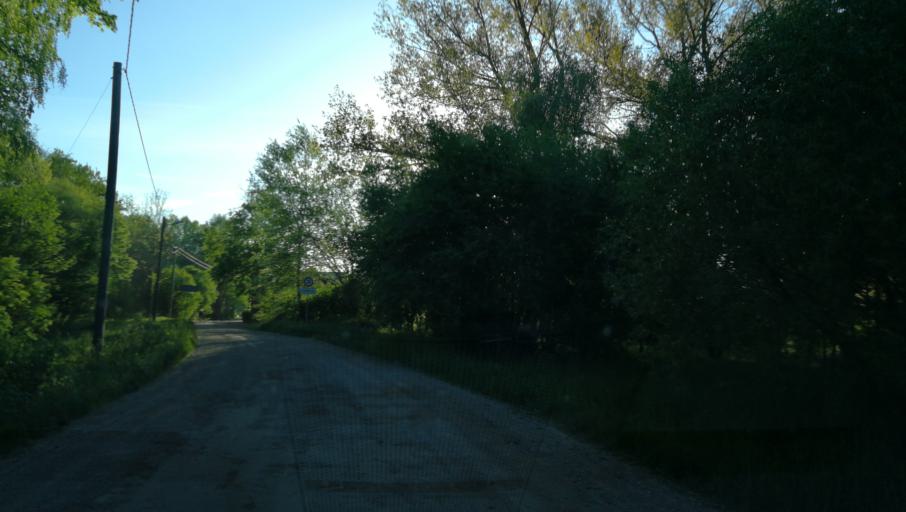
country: LV
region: Dobeles Rajons
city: Dobele
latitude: 56.6206
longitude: 23.2932
